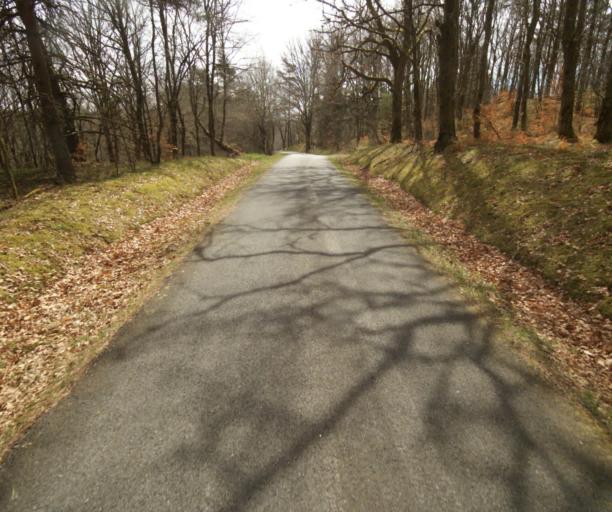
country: FR
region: Limousin
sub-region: Departement de la Correze
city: Egletons
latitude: 45.3716
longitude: 1.9675
